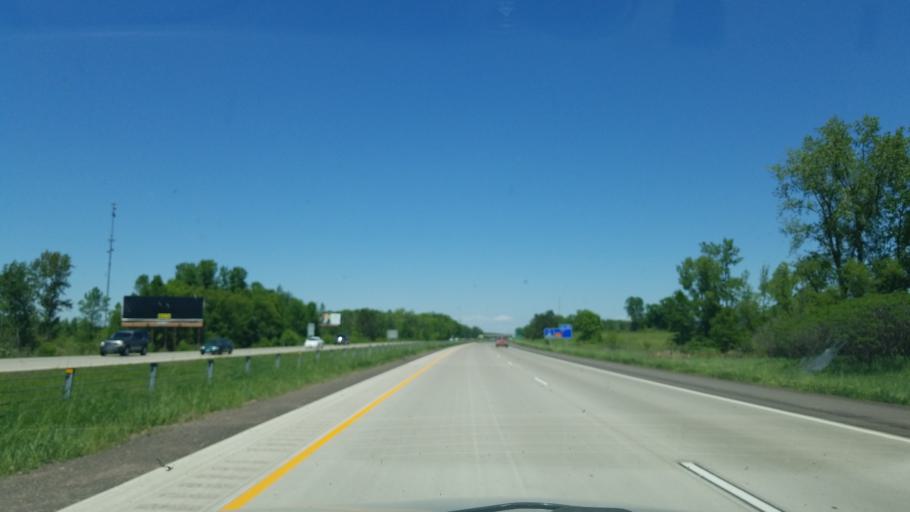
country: US
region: Minnesota
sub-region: Pine County
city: Pine City
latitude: 45.8358
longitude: -92.9812
